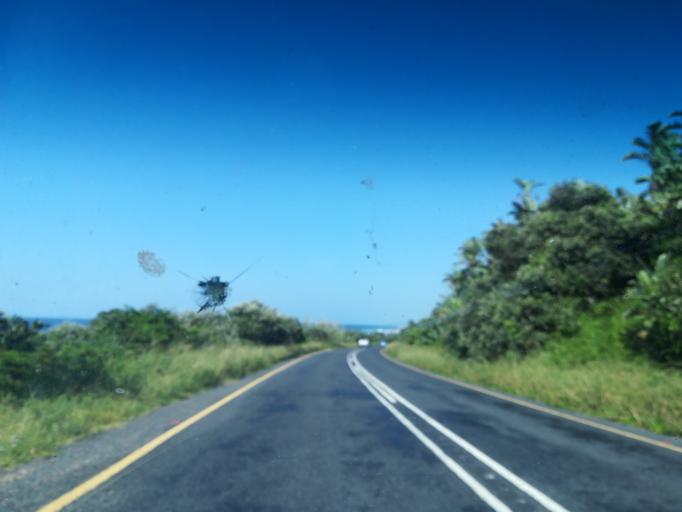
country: ZA
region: KwaZulu-Natal
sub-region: Ugu District Municipality
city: Scottburgh
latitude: -30.3410
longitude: 30.7311
